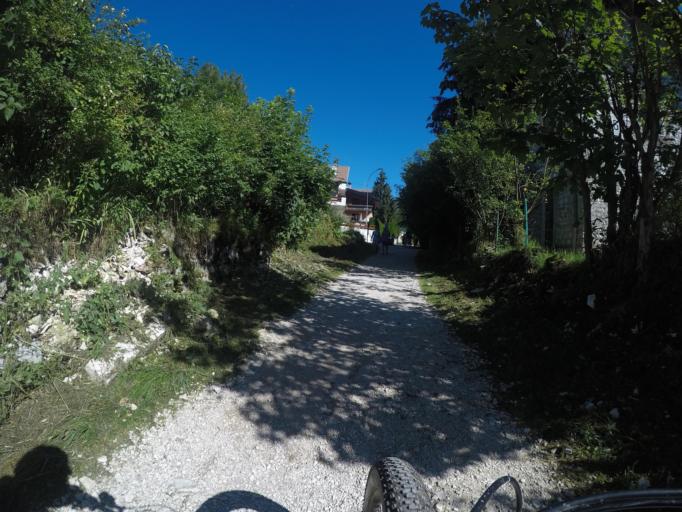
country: IT
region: Veneto
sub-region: Provincia di Vicenza
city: Canove di Roana
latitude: 45.8560
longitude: 11.4733
